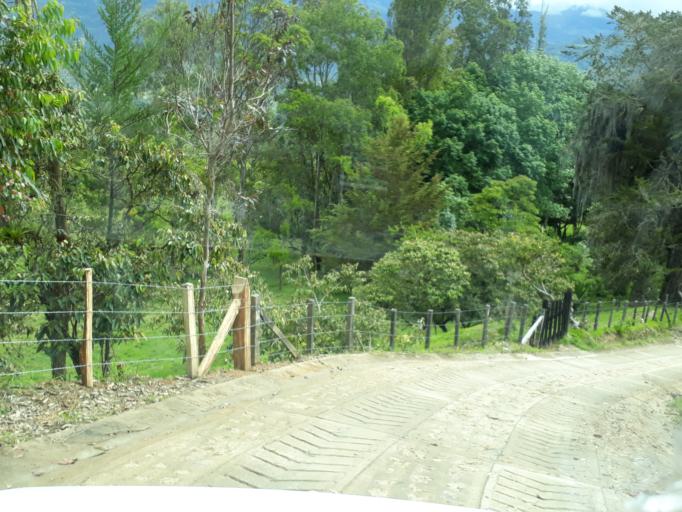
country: CO
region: Cundinamarca
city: Gacheta
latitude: 4.8056
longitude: -73.6468
